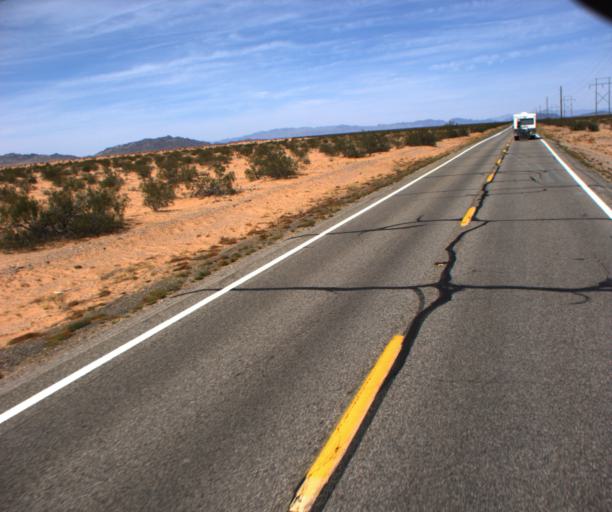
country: US
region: Arizona
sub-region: La Paz County
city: Quartzsite
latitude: 33.9016
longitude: -114.2169
